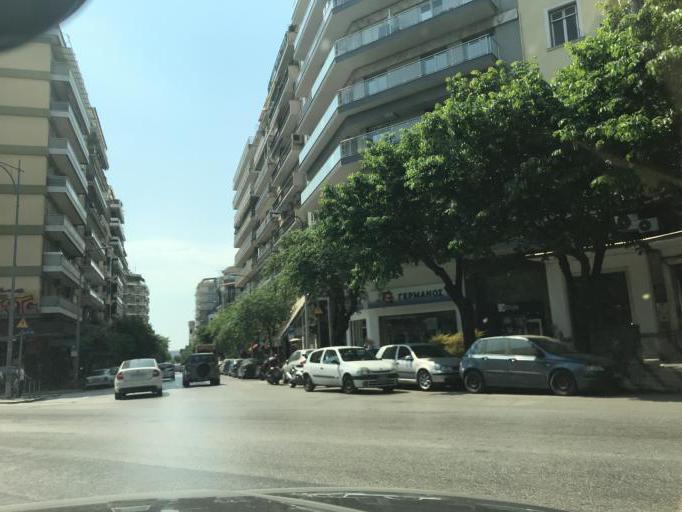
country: GR
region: Central Macedonia
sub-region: Nomos Thessalonikis
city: Agios Pavlos
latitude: 40.6296
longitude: 22.9479
